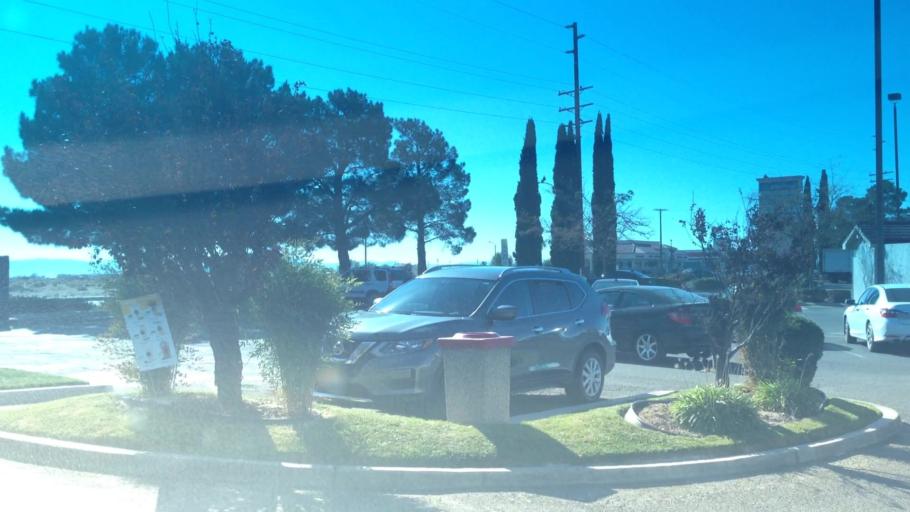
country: US
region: California
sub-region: Kern County
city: Rosamond
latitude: 34.8646
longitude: -118.1765
